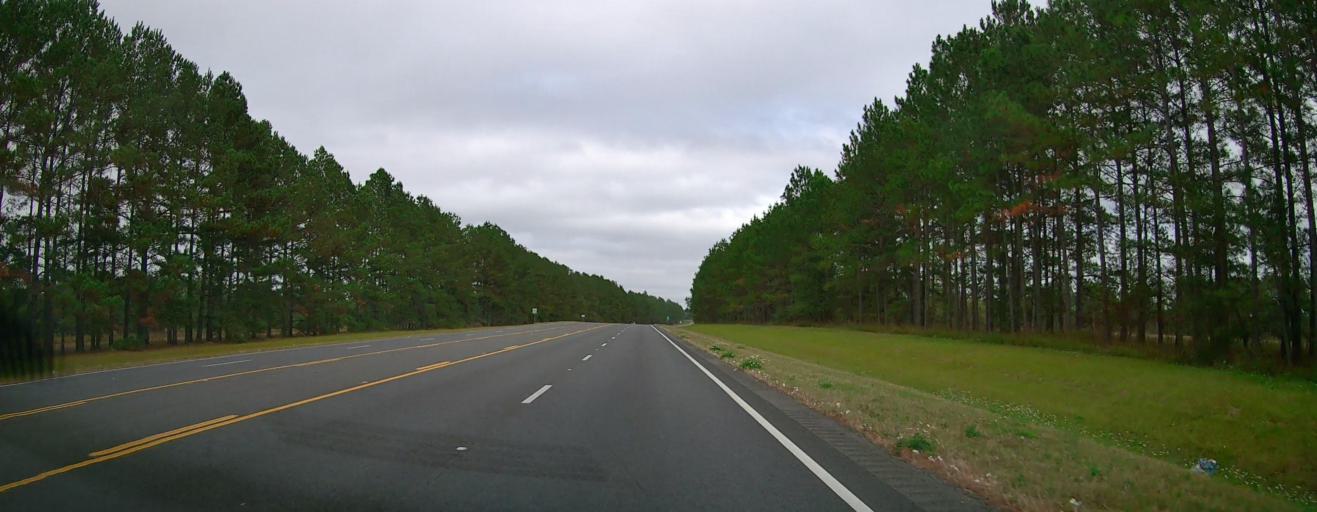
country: US
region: Georgia
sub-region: Colquitt County
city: Moultrie
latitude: 31.0374
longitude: -83.8516
